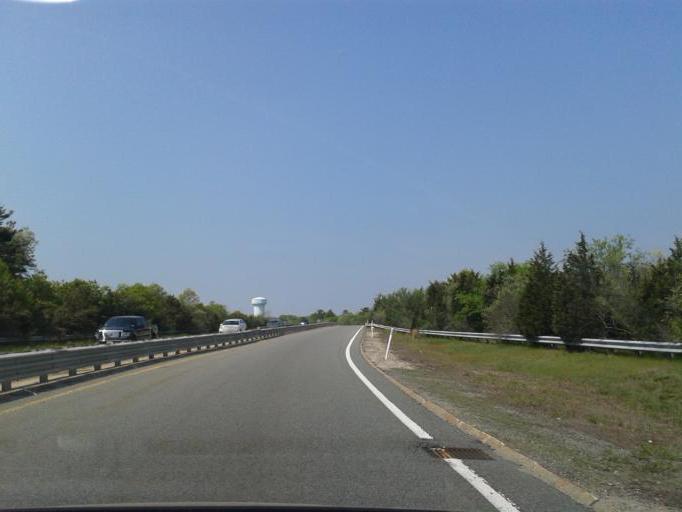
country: US
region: Massachusetts
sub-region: Barnstable County
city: Bourne
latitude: 41.7576
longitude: -70.5925
